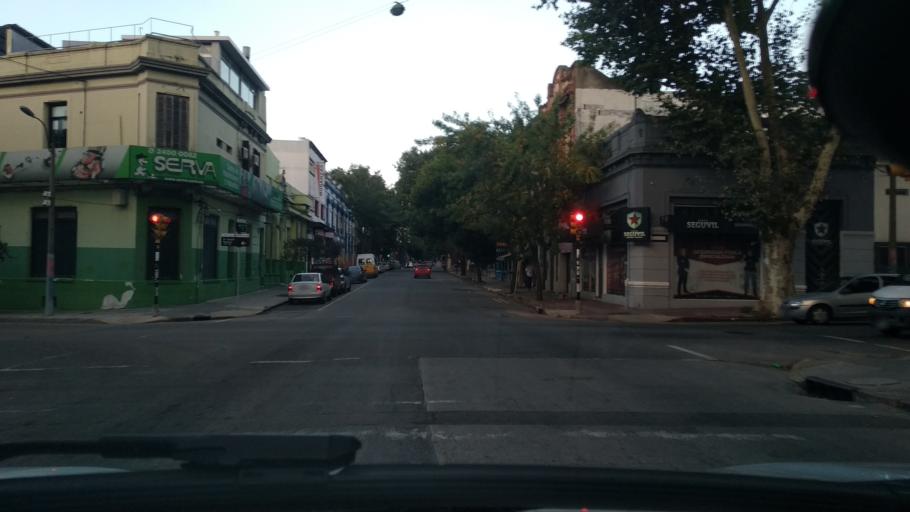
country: UY
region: Montevideo
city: Montevideo
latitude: -34.8974
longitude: -56.1712
